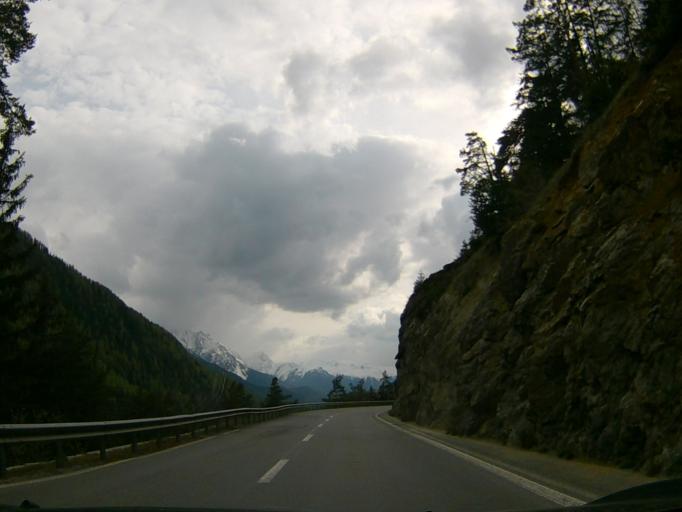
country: CH
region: Grisons
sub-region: Inn District
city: Scuol
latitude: 46.8351
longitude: 10.4041
